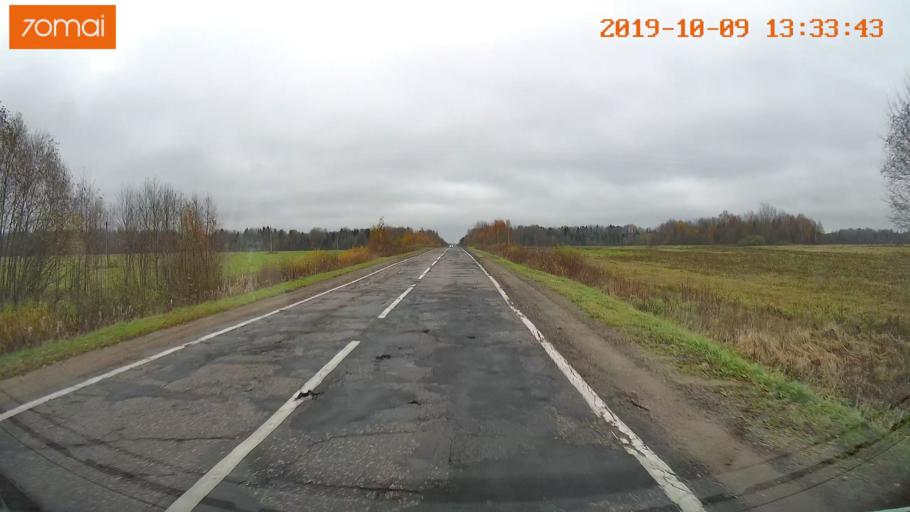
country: RU
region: Jaroslavl
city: Lyubim
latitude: 58.3268
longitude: 41.0512
